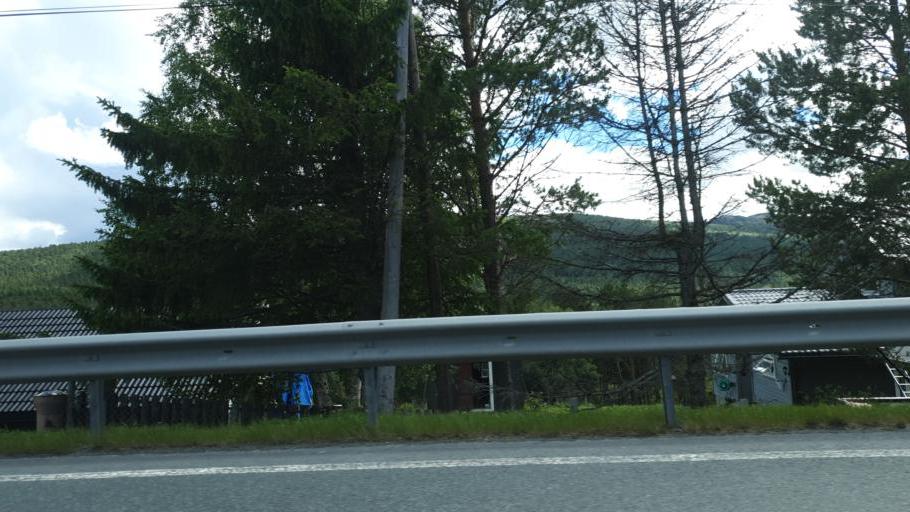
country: NO
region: Sor-Trondelag
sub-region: Rennebu
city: Berkak
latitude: 62.6796
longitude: 9.9233
